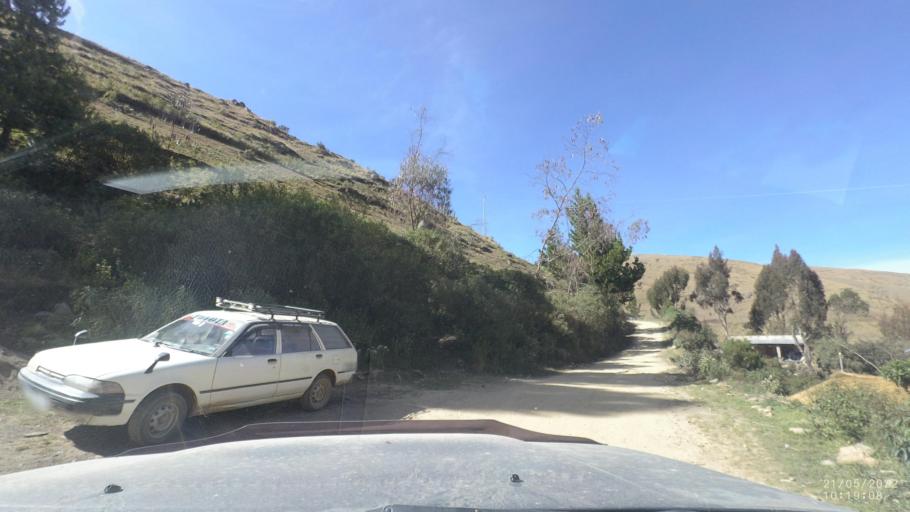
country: BO
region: Cochabamba
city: Colomi
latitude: -17.3259
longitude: -65.9596
